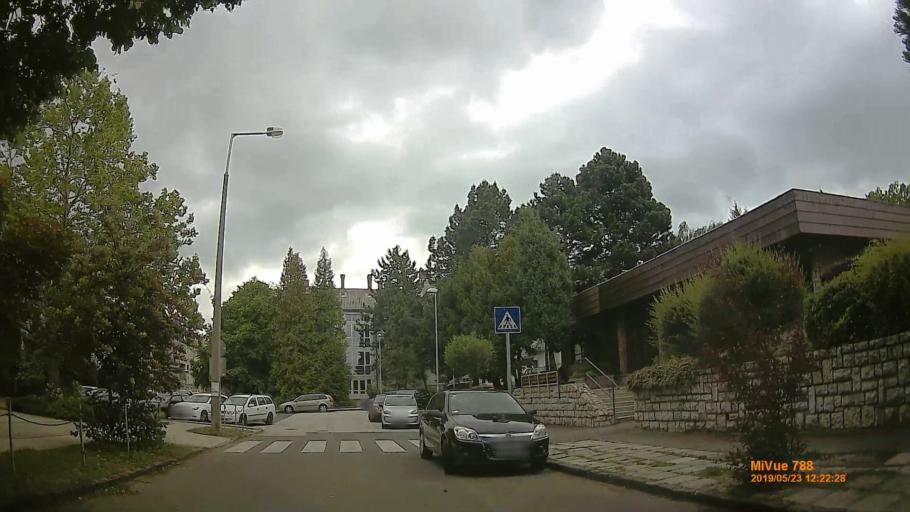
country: HU
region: Veszprem
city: Veszprem
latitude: 47.0848
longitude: 17.9057
